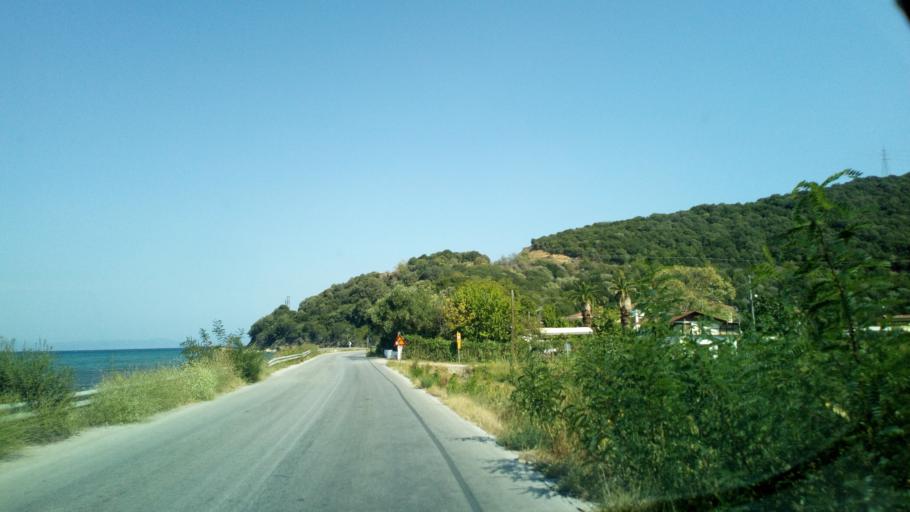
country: GR
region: Central Macedonia
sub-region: Nomos Thessalonikis
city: Stavros
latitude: 40.6580
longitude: 23.7297
